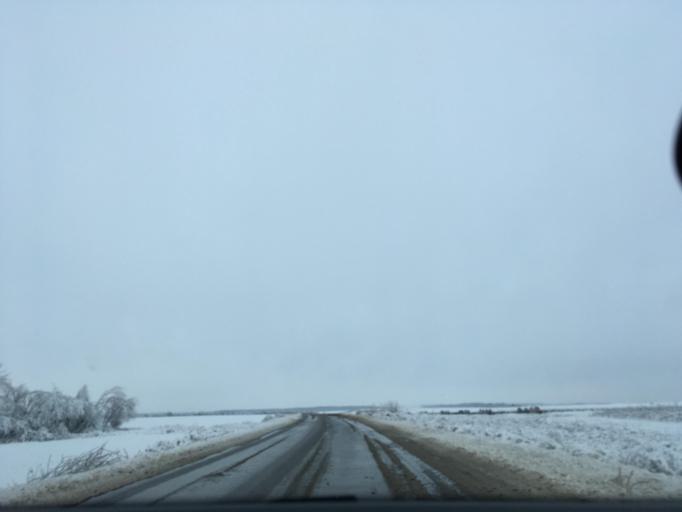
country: RU
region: Voronezj
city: Ol'khovatka
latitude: 50.1303
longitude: 39.1938
